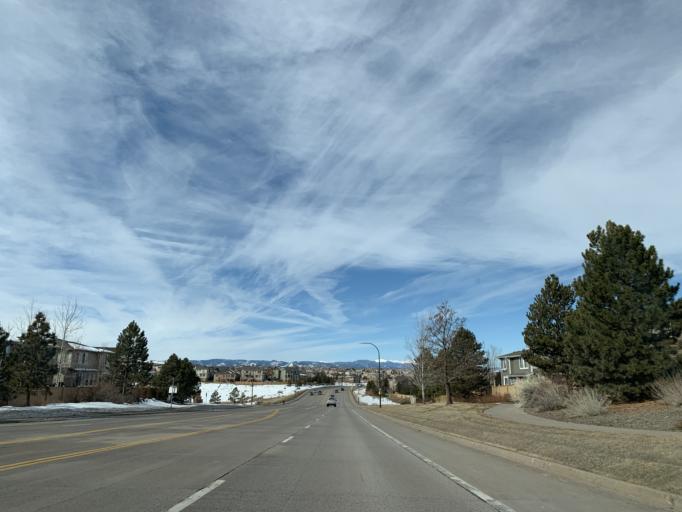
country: US
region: Colorado
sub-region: Douglas County
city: Carriage Club
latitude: 39.5217
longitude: -104.9257
